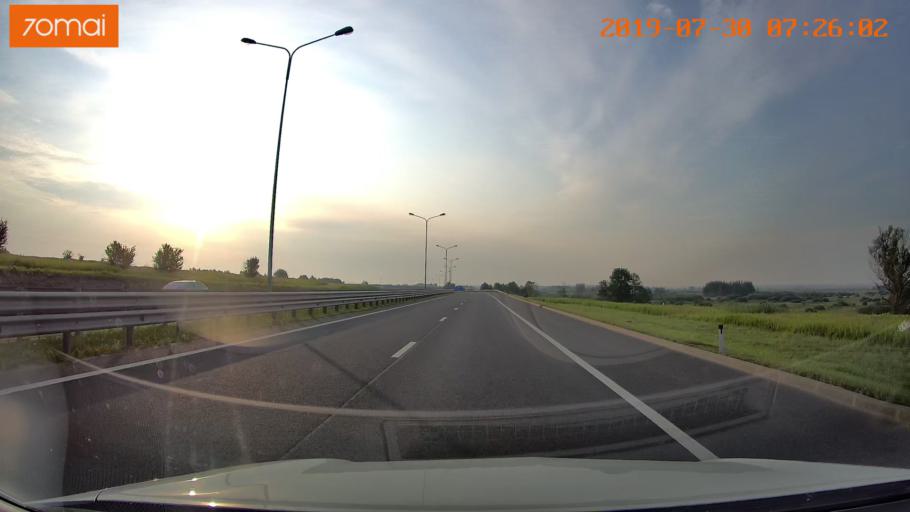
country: RU
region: Kaliningrad
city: Gvardeysk
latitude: 54.6840
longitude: 20.8503
